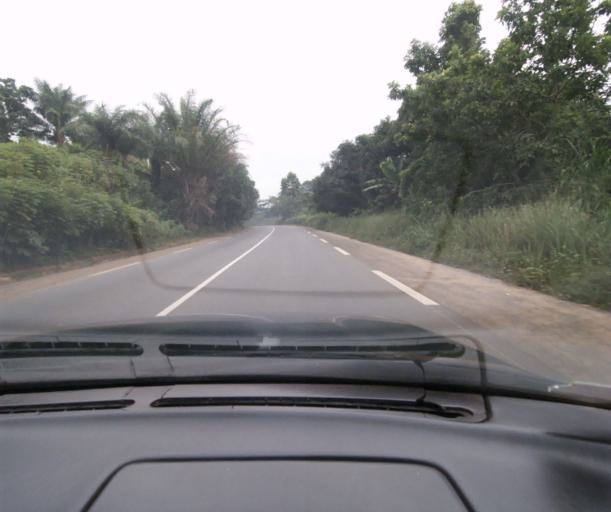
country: CM
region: Centre
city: Obala
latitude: 4.2085
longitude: 11.4475
